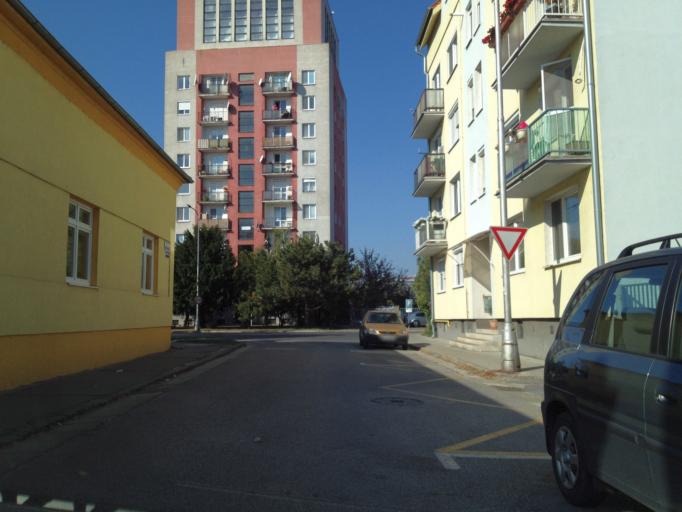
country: SK
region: Nitriansky
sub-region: Okres Nove Zamky
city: Nove Zamky
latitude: 47.9854
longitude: 18.1616
